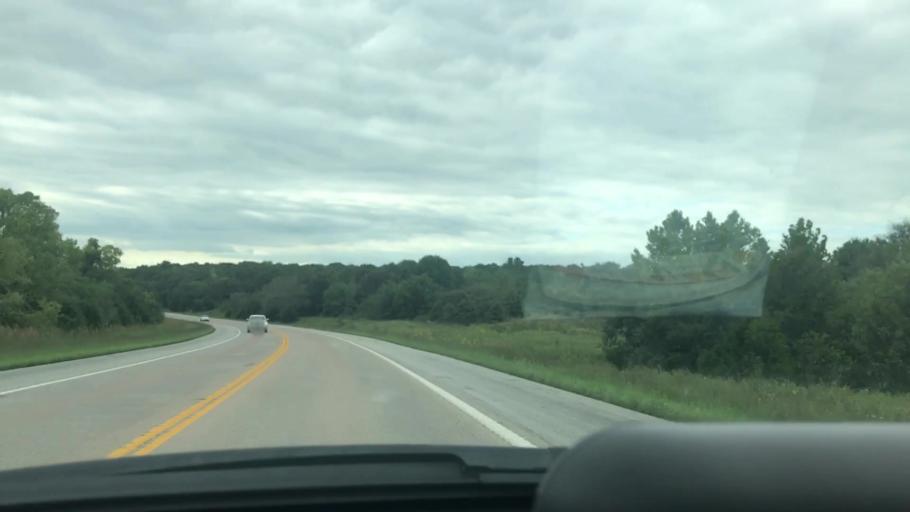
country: US
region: Missouri
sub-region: Benton County
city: Warsaw
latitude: 38.2068
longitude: -93.3285
